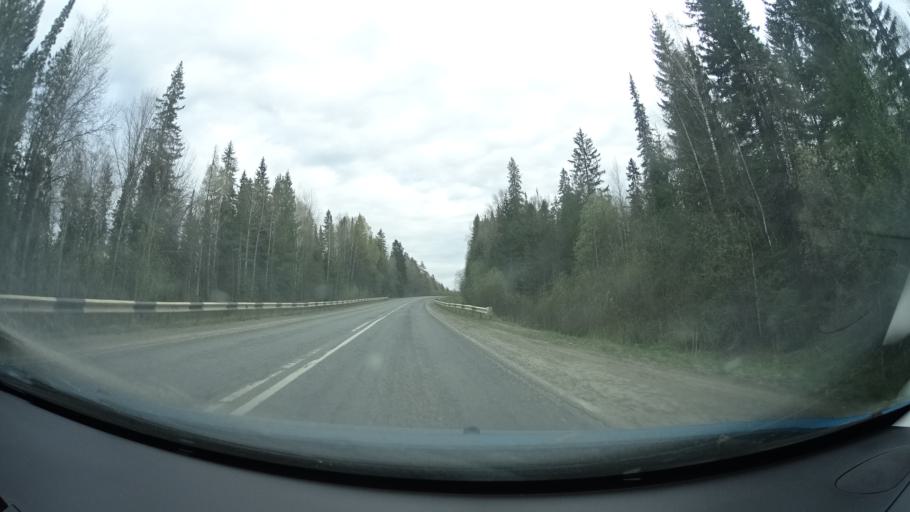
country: RU
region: Perm
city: Yugo-Kamskiy
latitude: 57.6636
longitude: 55.5935
